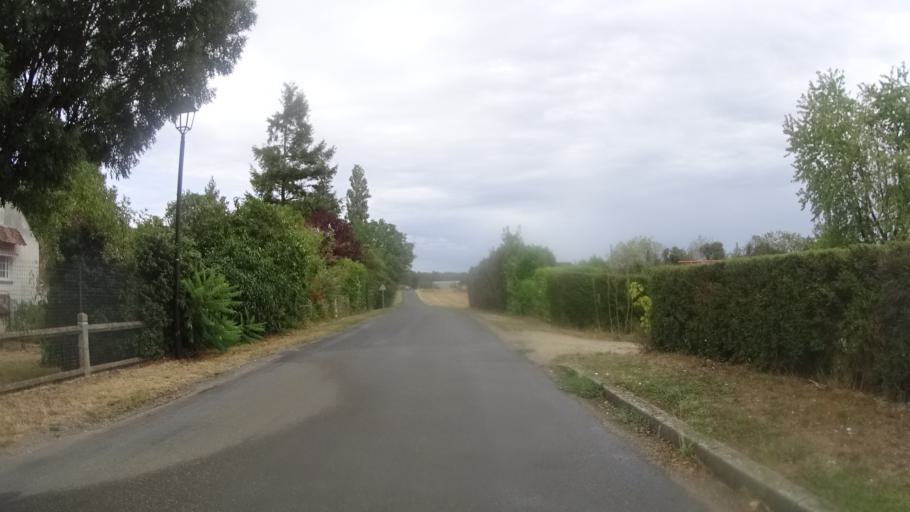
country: FR
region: Centre
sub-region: Departement du Loiret
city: Boynes
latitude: 48.1864
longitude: 2.3793
